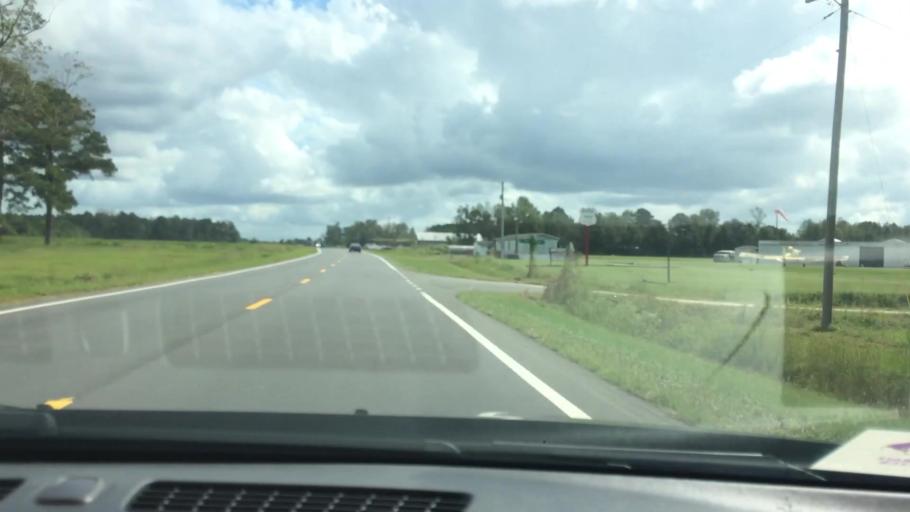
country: US
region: North Carolina
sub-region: Pitt County
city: Farmville
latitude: 35.5607
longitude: -77.5607
